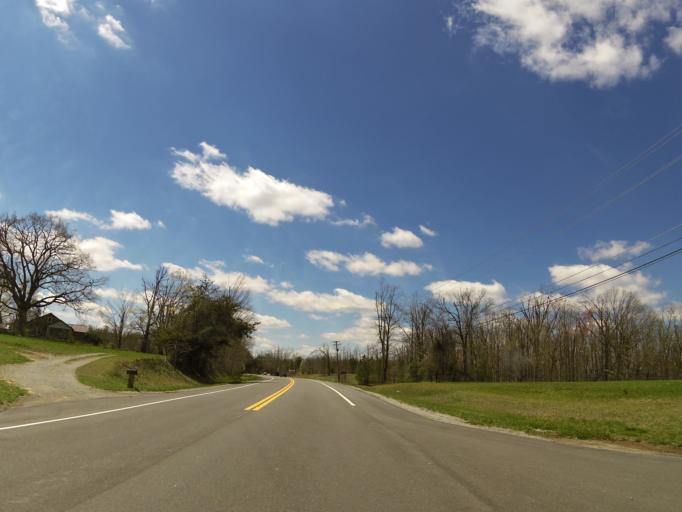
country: US
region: Tennessee
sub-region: Putnam County
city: Monterey
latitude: 35.9675
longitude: -85.2315
